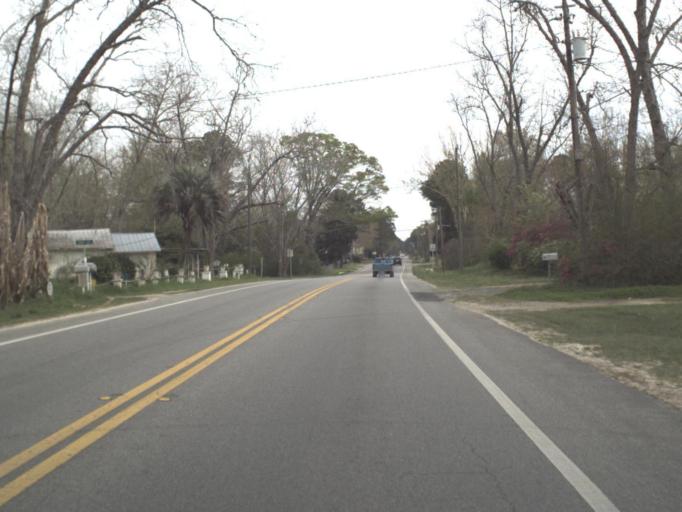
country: US
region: Florida
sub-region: Holmes County
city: Bonifay
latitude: 30.8044
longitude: -85.6781
